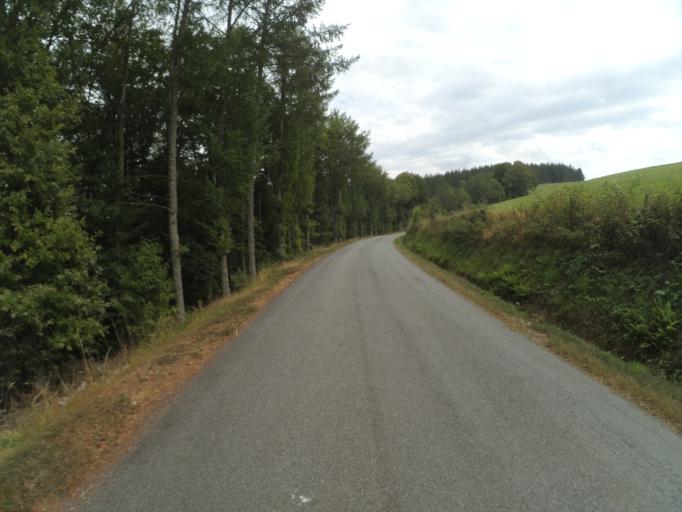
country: FR
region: Limousin
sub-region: Departement de la Correze
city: Meymac
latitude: 45.6581
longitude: 2.1087
